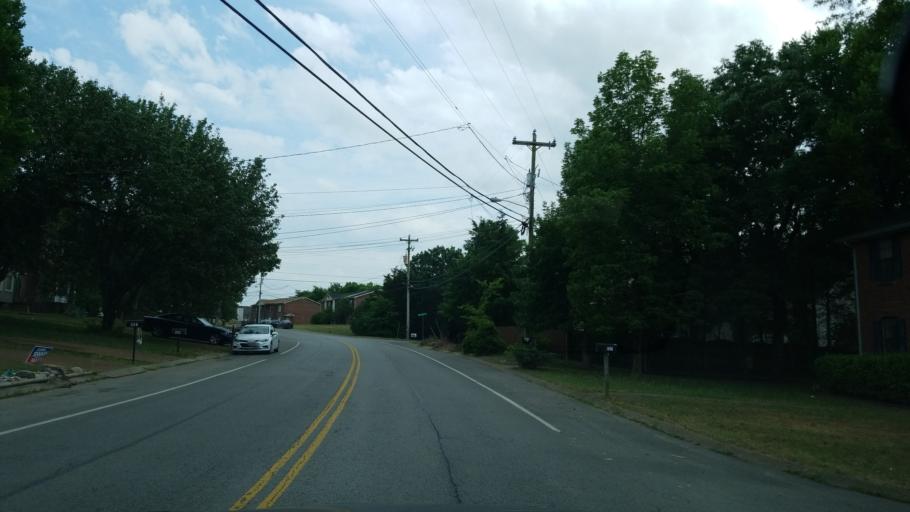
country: US
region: Tennessee
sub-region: Rutherford County
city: La Vergne
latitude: 36.0829
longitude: -86.6123
